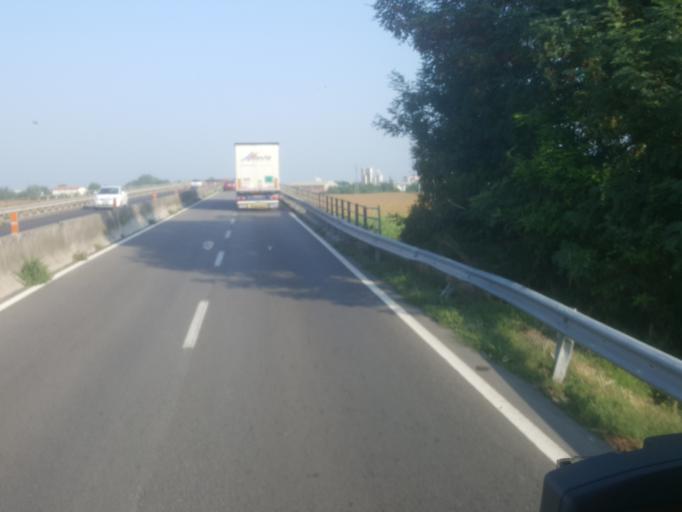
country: IT
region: Emilia-Romagna
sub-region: Provincia di Ravenna
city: Fornace Zarattini
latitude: 44.4187
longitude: 12.1668
